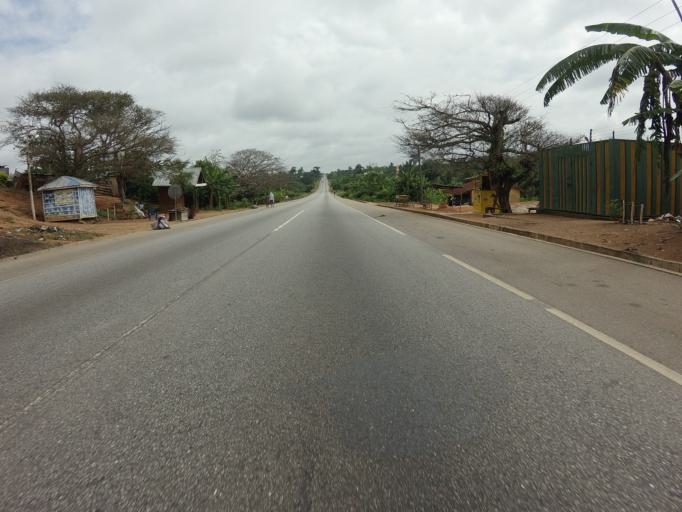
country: GH
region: Ashanti
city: Mampong
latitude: 7.0541
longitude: -1.7110
